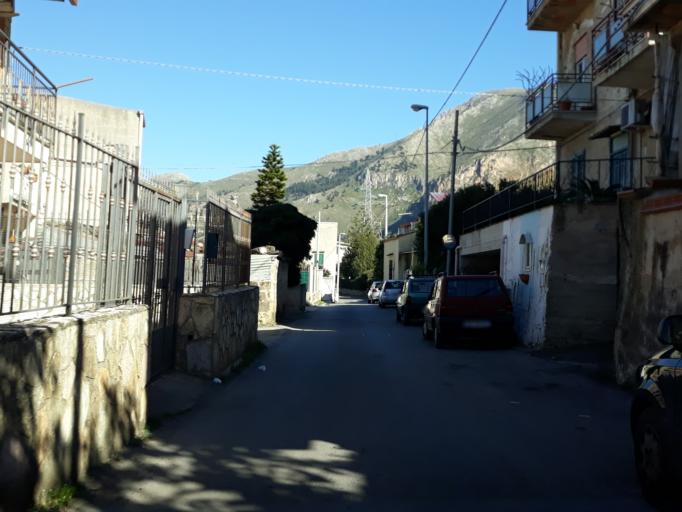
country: IT
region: Sicily
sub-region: Palermo
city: Villa Ciambra
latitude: 38.0750
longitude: 13.3545
